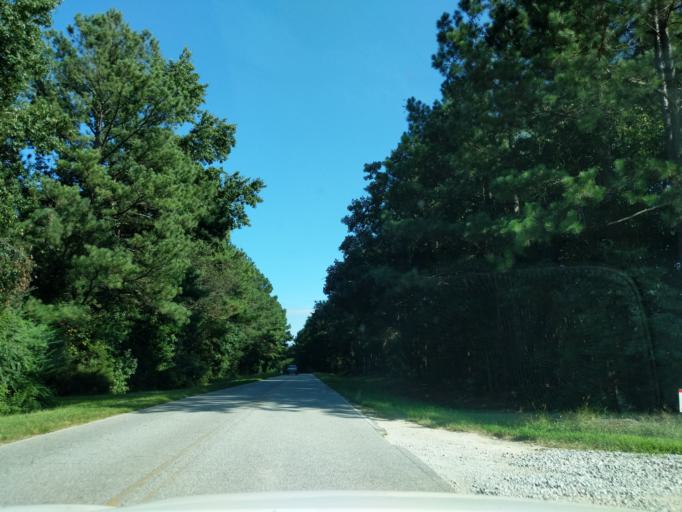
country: US
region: Georgia
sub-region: Oglethorpe County
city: Lexington
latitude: 33.9279
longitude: -83.0384
